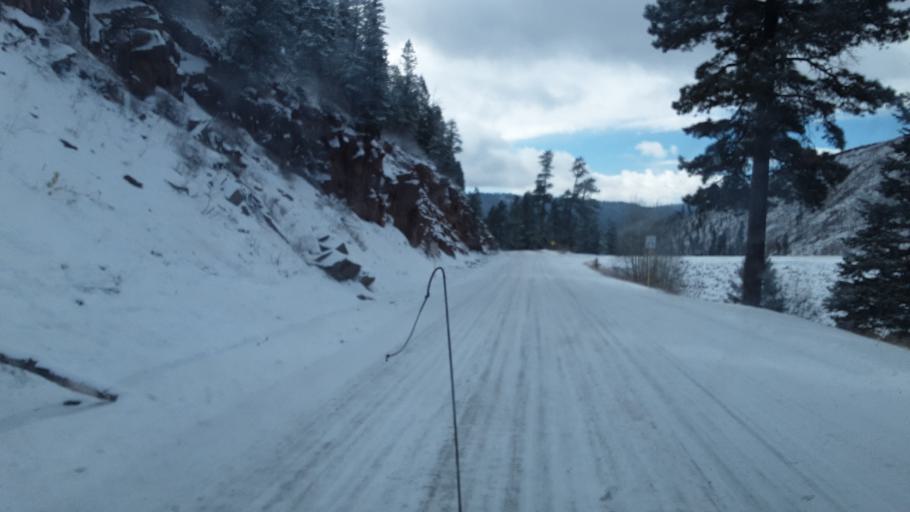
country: US
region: Colorado
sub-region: La Plata County
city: Bayfield
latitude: 37.3824
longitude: -107.6581
